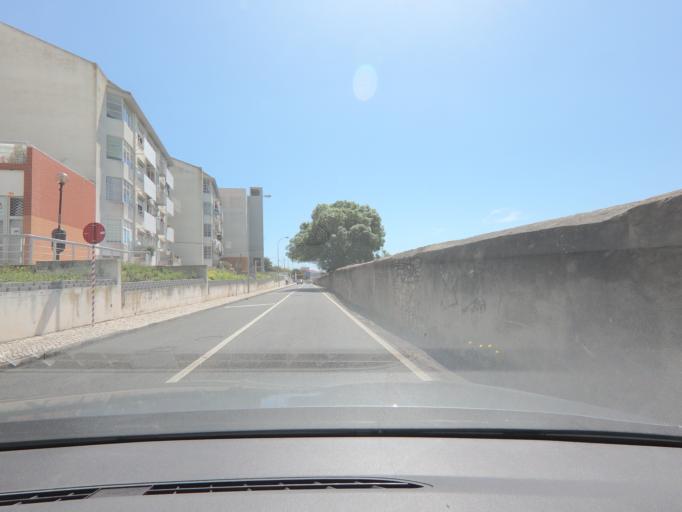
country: PT
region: Lisbon
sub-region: Oeiras
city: Oeiras
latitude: 38.6972
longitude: -9.3120
